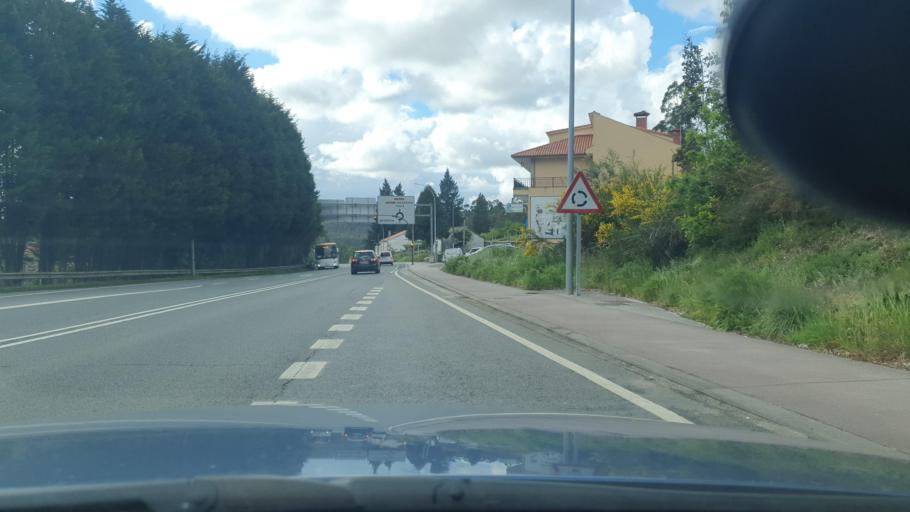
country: ES
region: Galicia
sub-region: Provincia da Coruna
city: Santiago de Compostela
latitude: 42.8711
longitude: -8.5783
